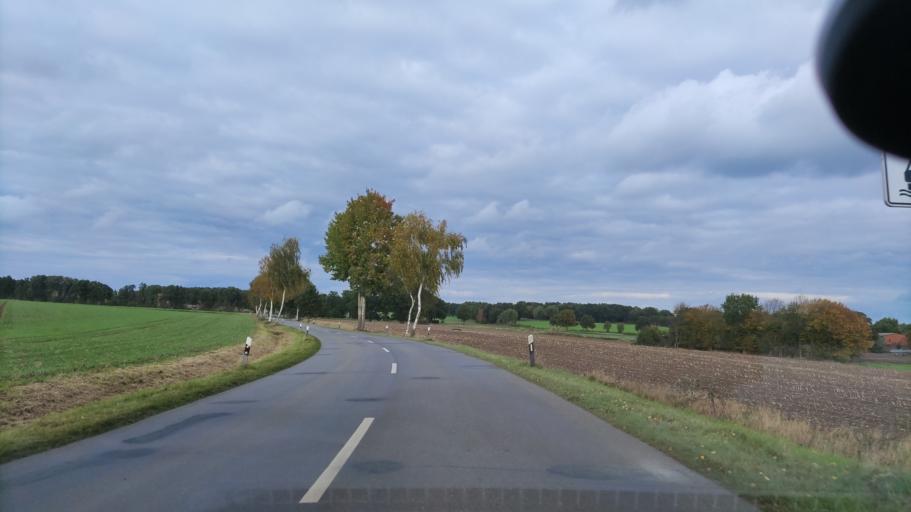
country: DE
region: Lower Saxony
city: Romstedt
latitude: 53.0783
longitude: 10.6361
